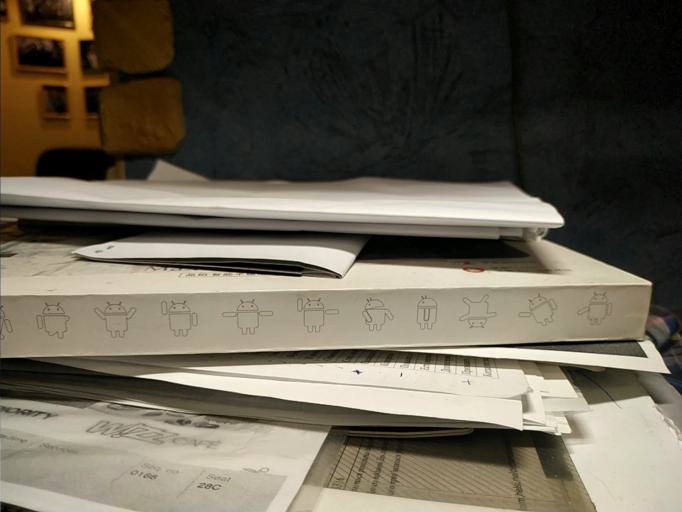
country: RU
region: Tverskaya
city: Zubtsov
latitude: 56.0855
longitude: 34.7722
